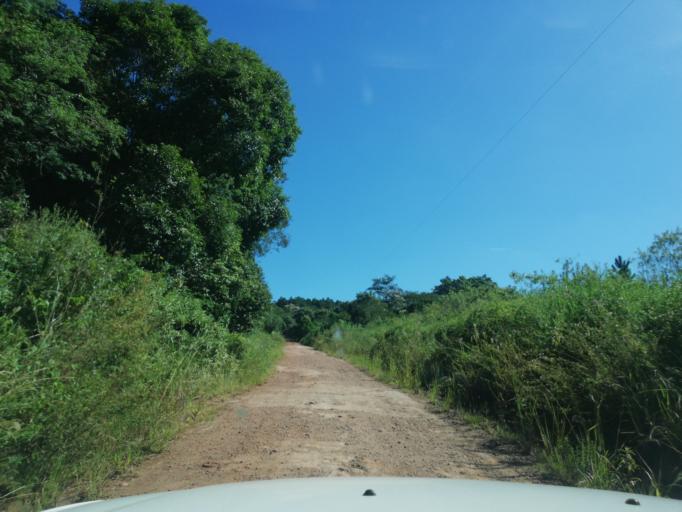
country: AR
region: Misiones
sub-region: Departamento de Leandro N. Alem
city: Leandro N. Alem
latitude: -27.5787
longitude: -55.3732
